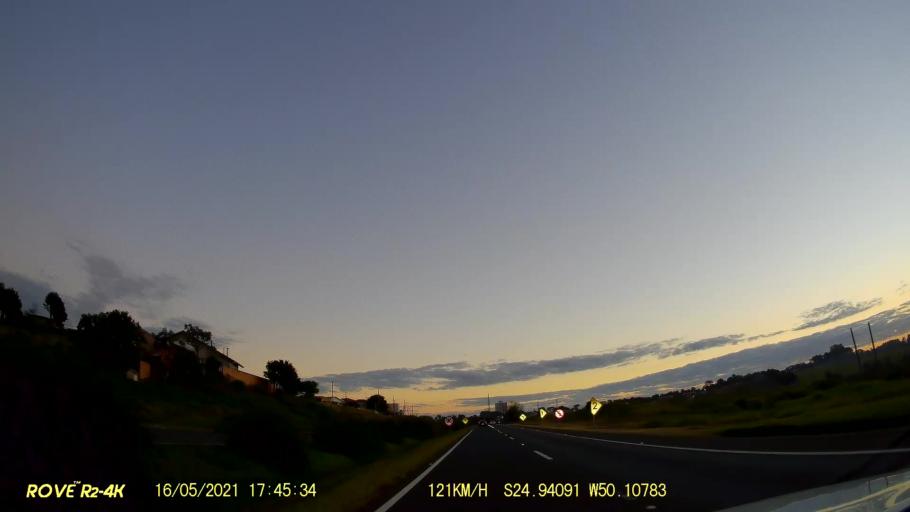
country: BR
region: Parana
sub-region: Carambei
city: Carambei
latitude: -24.9405
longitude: -50.1074
